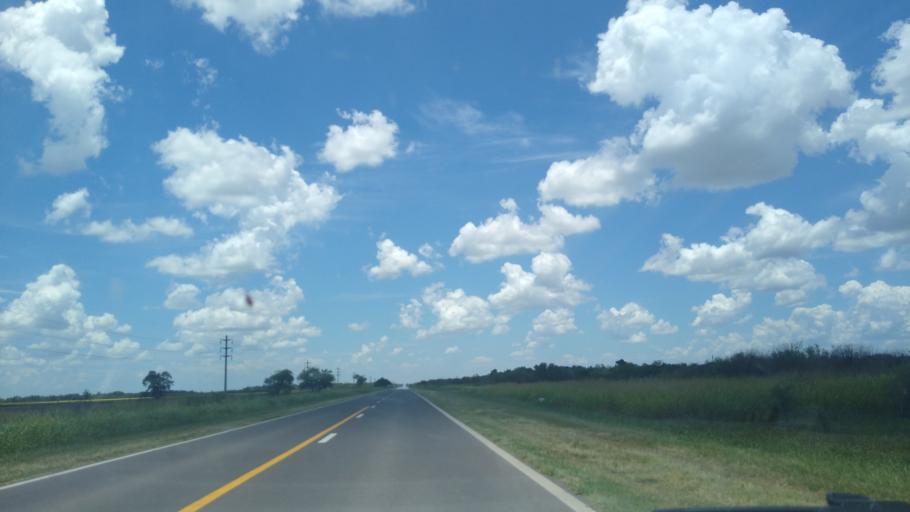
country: AR
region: Chaco
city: Presidencia Roque Saenz Pena
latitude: -26.7373
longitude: -60.3854
